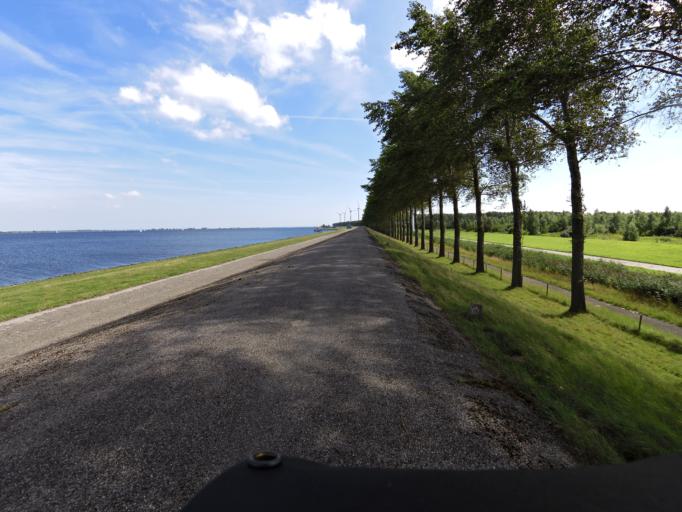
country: NL
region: South Holland
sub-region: Gemeente Goeree-Overflakkee
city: Middelharnis
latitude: 51.7614
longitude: 4.2092
